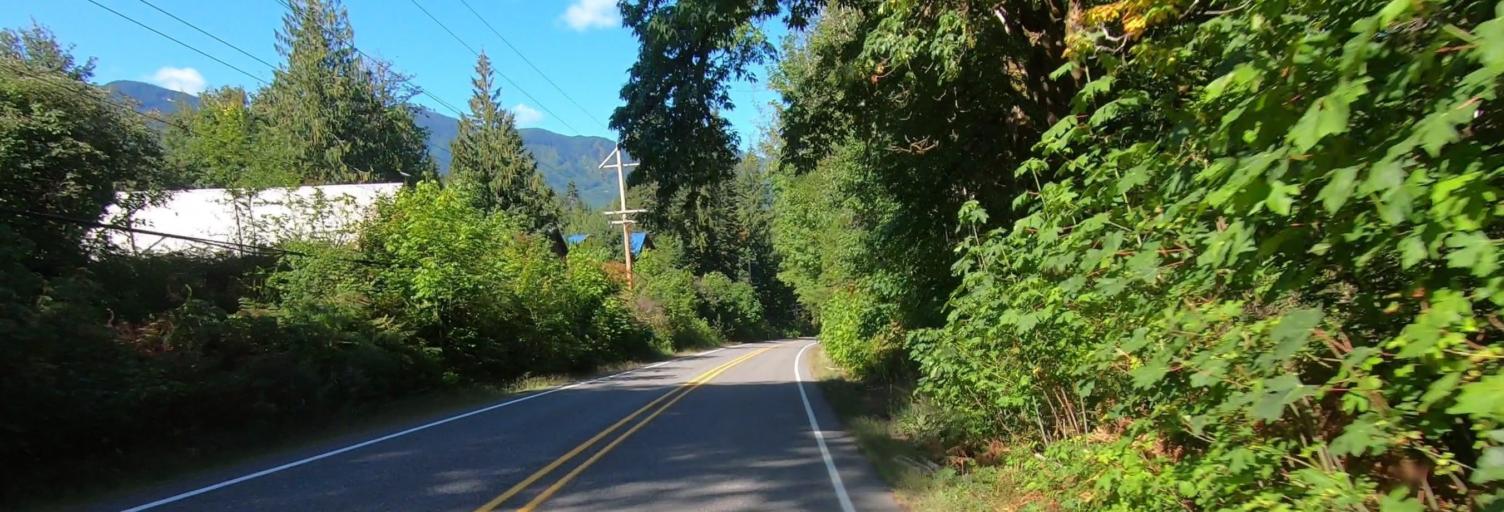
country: US
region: Washington
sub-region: Whatcom County
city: Peaceful Valley
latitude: 48.8908
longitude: -121.9378
